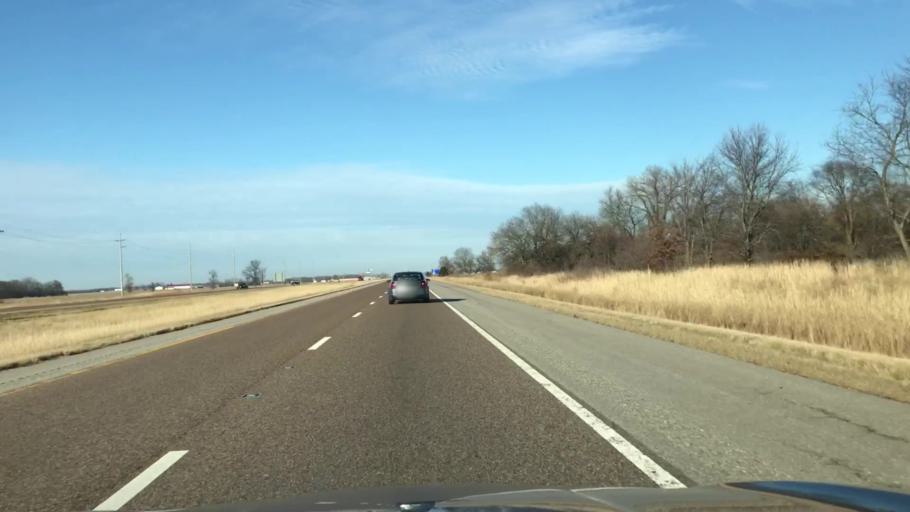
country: US
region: Illinois
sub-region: Macoupin County
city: Staunton
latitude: 38.9890
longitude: -89.7494
